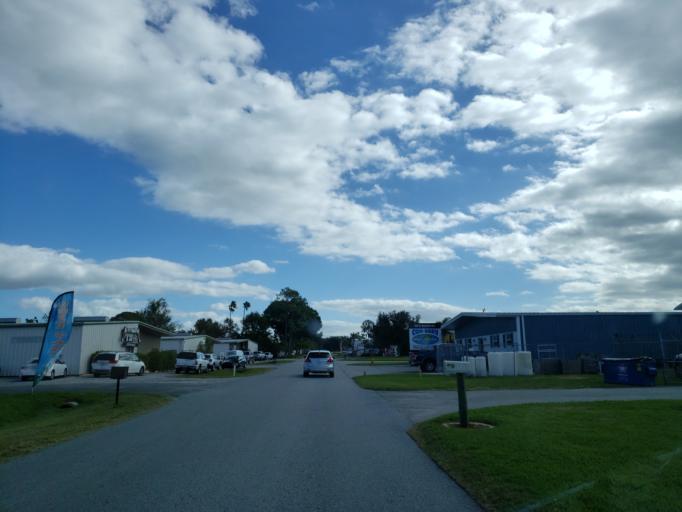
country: US
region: Florida
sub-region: Polk County
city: Medulla
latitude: 27.9614
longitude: -81.9642
